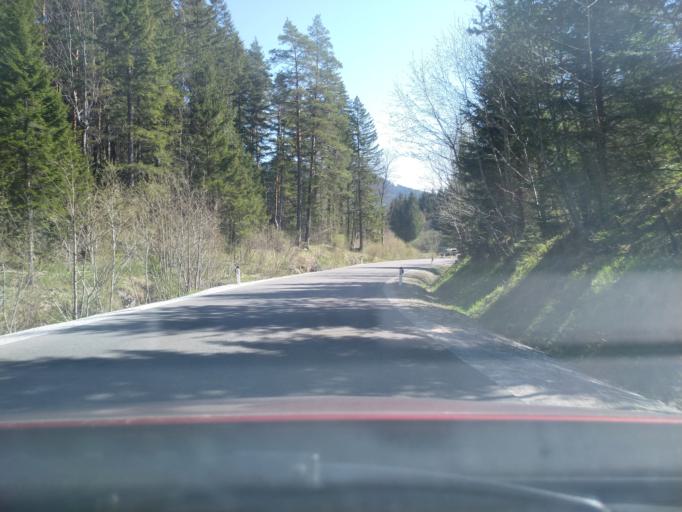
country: AT
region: Lower Austria
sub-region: Politischer Bezirk Wiener Neustadt
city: Gutenstein
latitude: 47.8227
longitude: 15.8243
